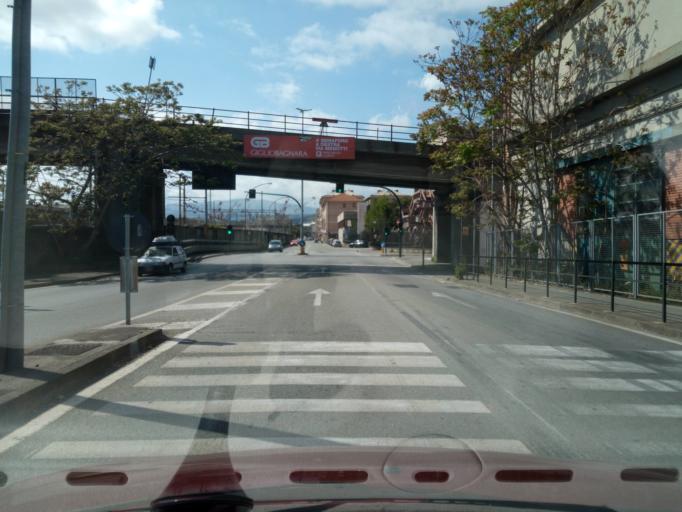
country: IT
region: Liguria
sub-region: Provincia di Genova
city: San Teodoro
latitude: 44.4214
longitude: 8.8527
